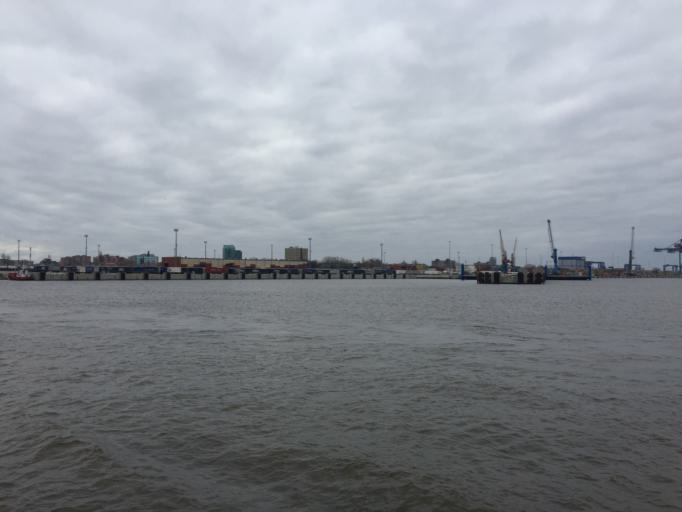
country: LT
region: Klaipedos apskritis
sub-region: Klaipeda
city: Klaipeda
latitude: 55.6874
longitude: 21.1341
